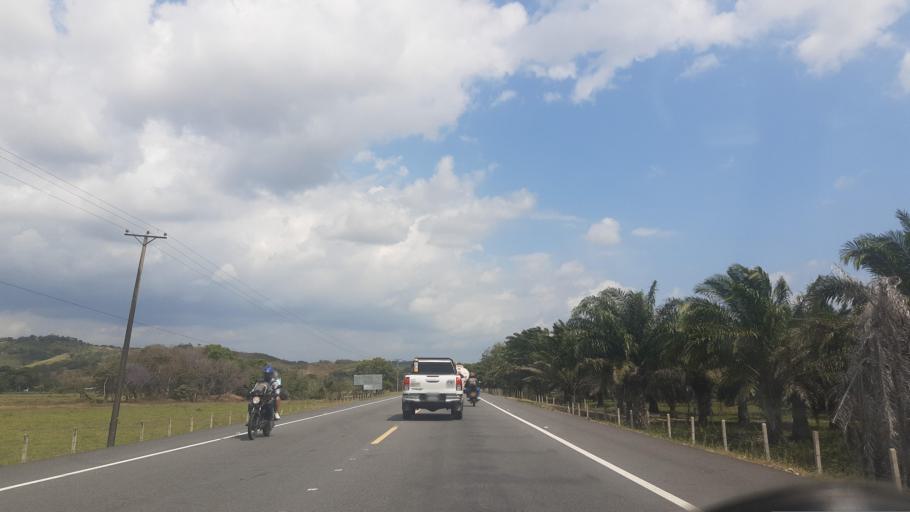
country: CO
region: Casanare
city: Tauramena
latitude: 4.9197
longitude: -72.6746
